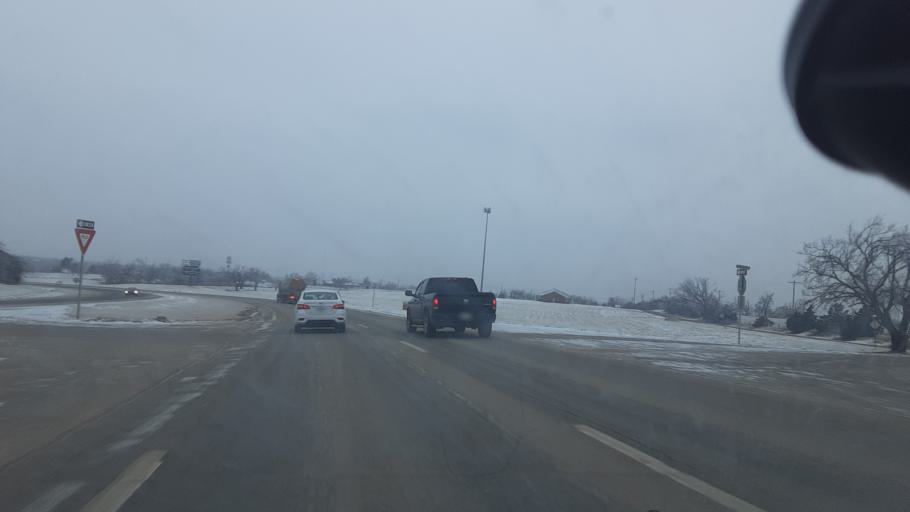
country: US
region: Oklahoma
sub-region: Logan County
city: Guthrie
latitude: 35.8845
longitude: -97.3828
